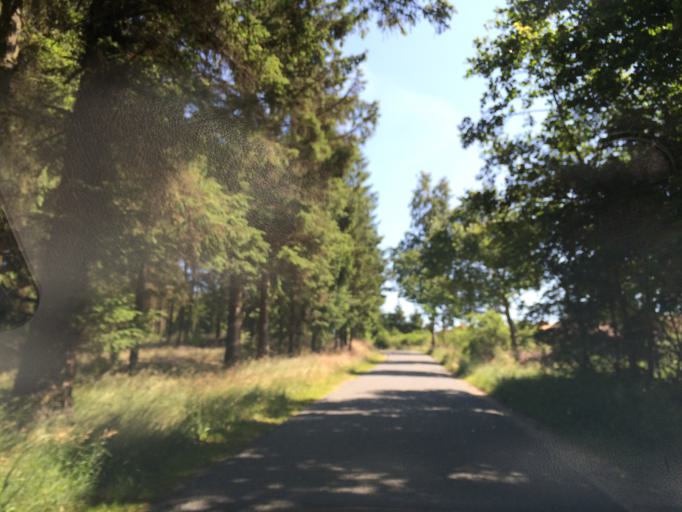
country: DK
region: Central Jutland
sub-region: Silkeborg Kommune
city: Svejbaek
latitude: 56.2103
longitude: 9.7093
